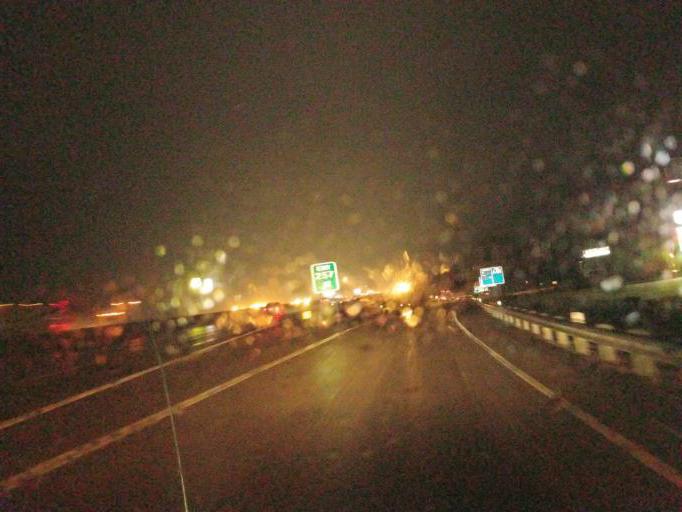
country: US
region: Missouri
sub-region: Franklin County
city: Pacific
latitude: 38.4850
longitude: -90.7567
